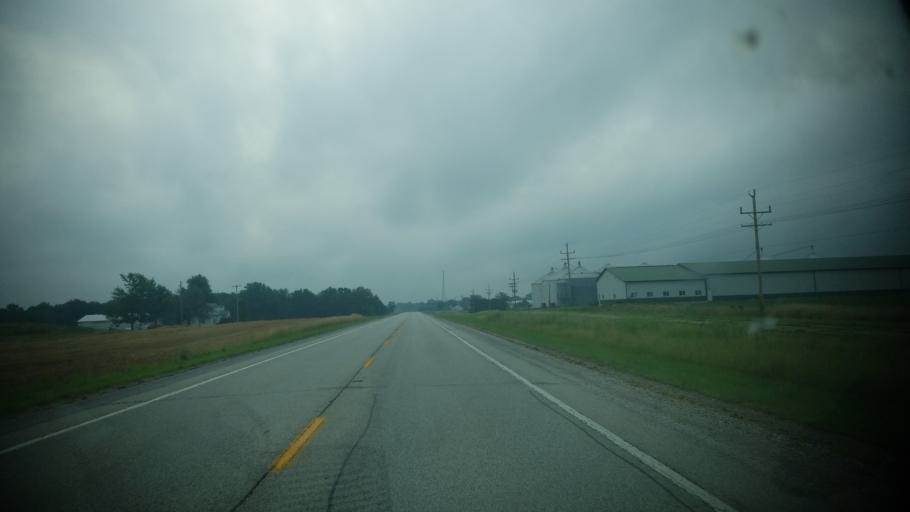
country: US
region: Illinois
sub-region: Clay County
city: Flora
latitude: 38.6778
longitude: -88.3750
